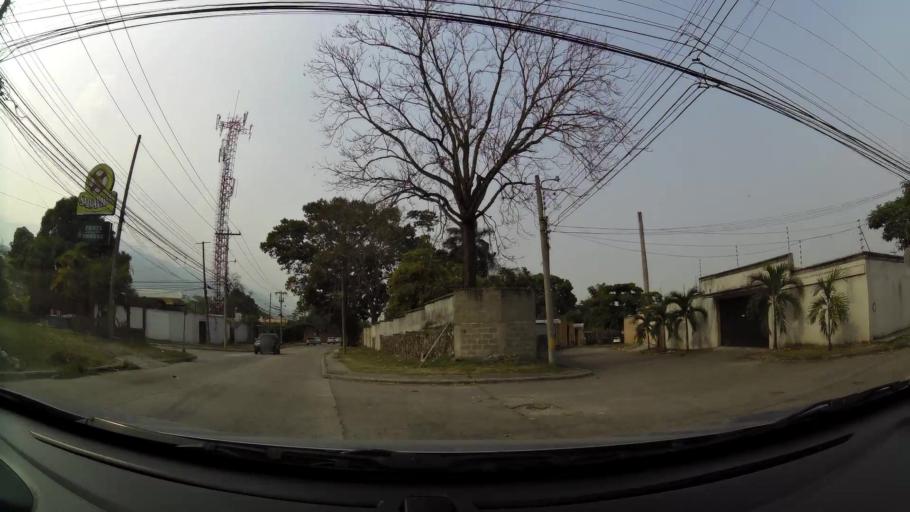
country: HN
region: Cortes
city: El Zapotal del Norte
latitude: 15.5093
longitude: -88.0439
